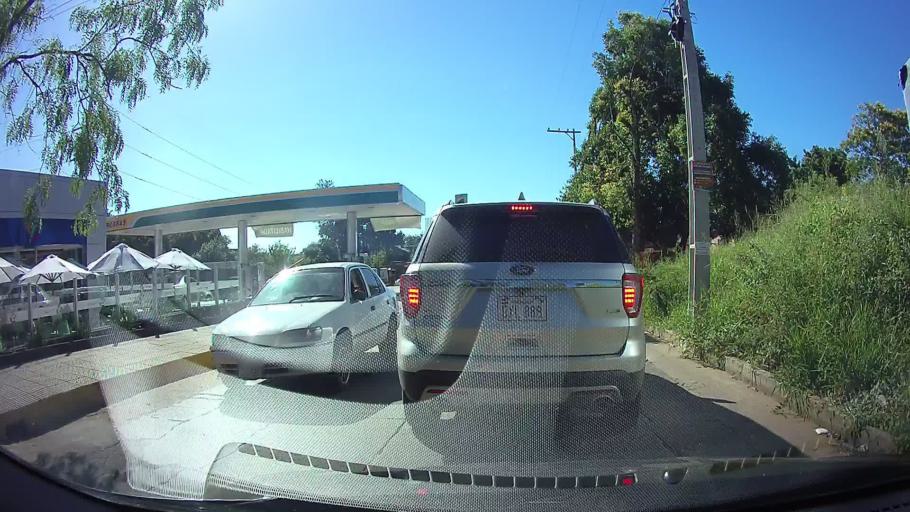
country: PY
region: Central
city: Fernando de la Mora
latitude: -25.2963
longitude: -57.5351
